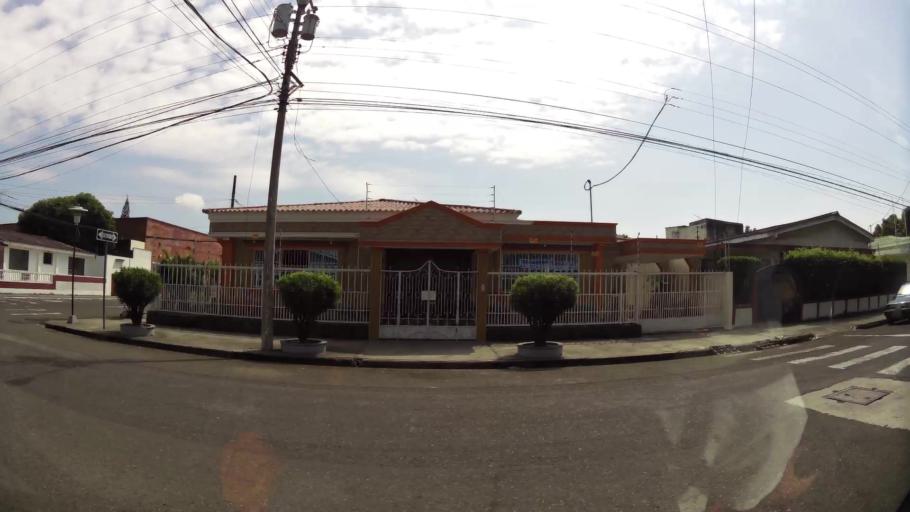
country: EC
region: Guayas
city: Guayaquil
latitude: -2.2317
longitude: -79.8937
